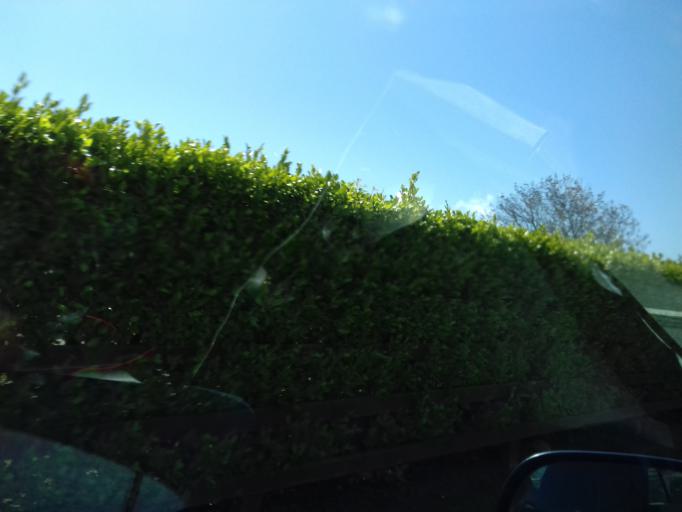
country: IE
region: Munster
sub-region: Waterford
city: Dunmore East
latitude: 52.1845
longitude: -6.8632
